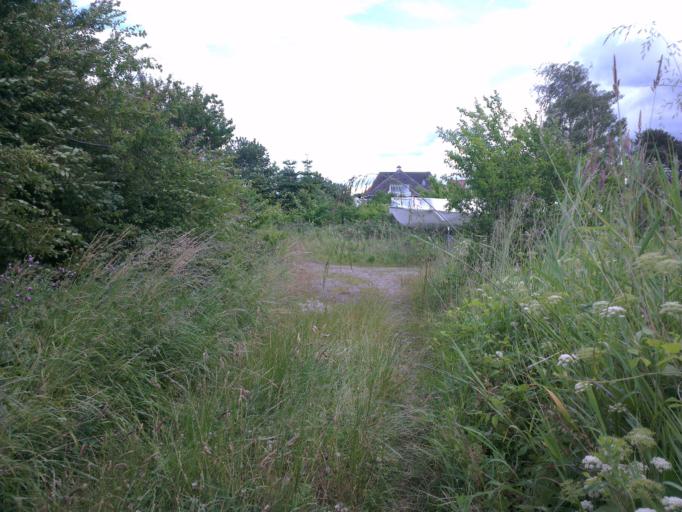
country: DK
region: Capital Region
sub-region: Frederikssund Kommune
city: Frederikssund
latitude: 55.8273
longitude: 12.0632
